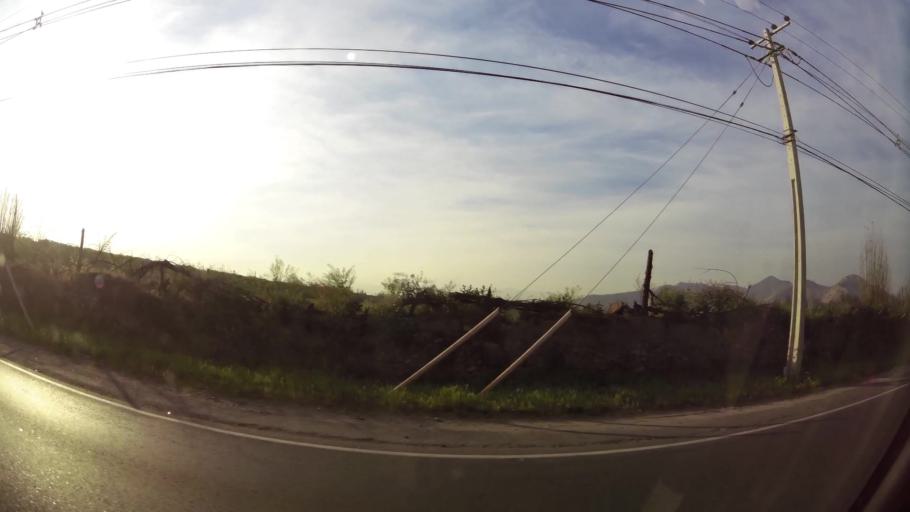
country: CL
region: Santiago Metropolitan
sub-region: Provincia de Maipo
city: San Bernardo
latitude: -33.5504
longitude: -70.7492
